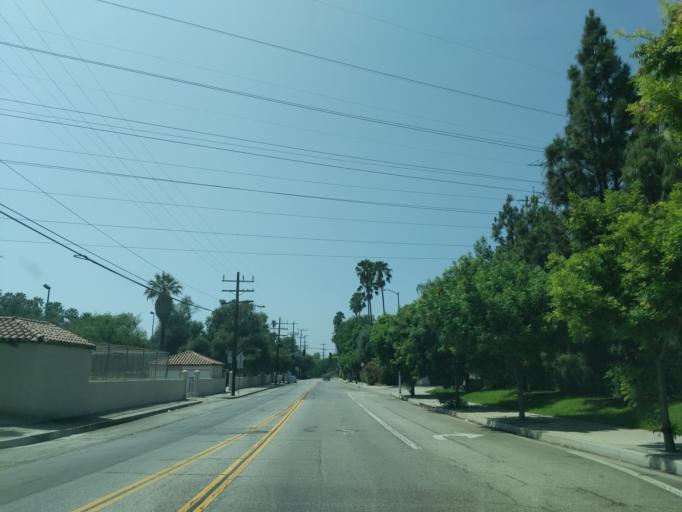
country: US
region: California
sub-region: Los Angeles County
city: San Fernando
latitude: 34.2728
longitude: -118.4596
